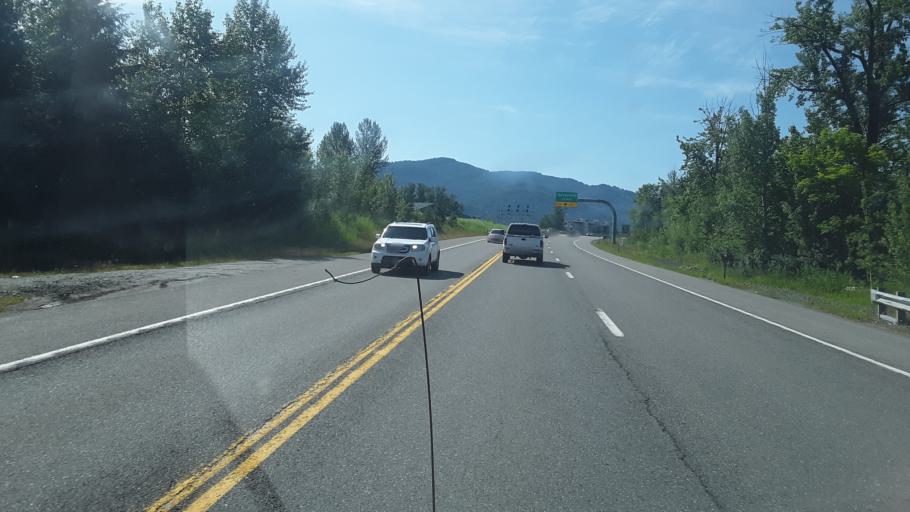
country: US
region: Idaho
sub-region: Bonner County
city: Sandpoint
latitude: 48.2828
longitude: -116.5491
